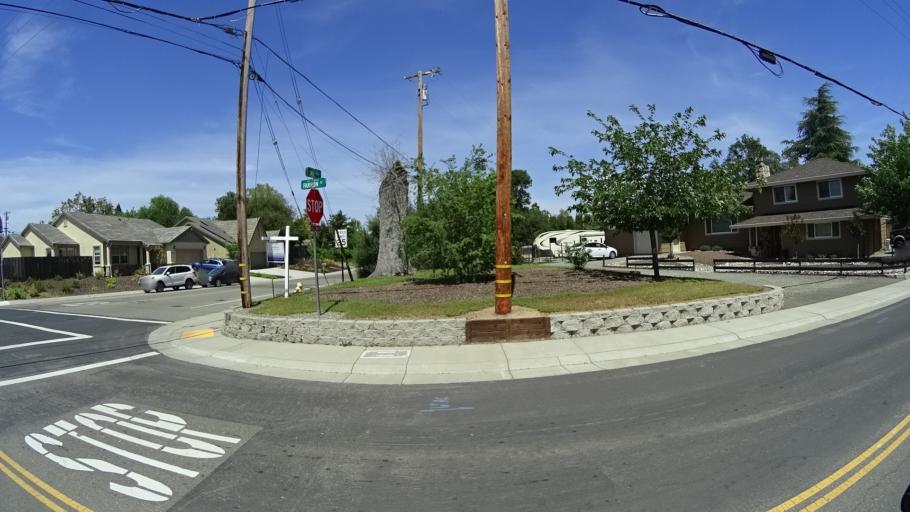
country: US
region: California
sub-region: Placer County
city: Rocklin
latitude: 38.7877
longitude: -121.2440
